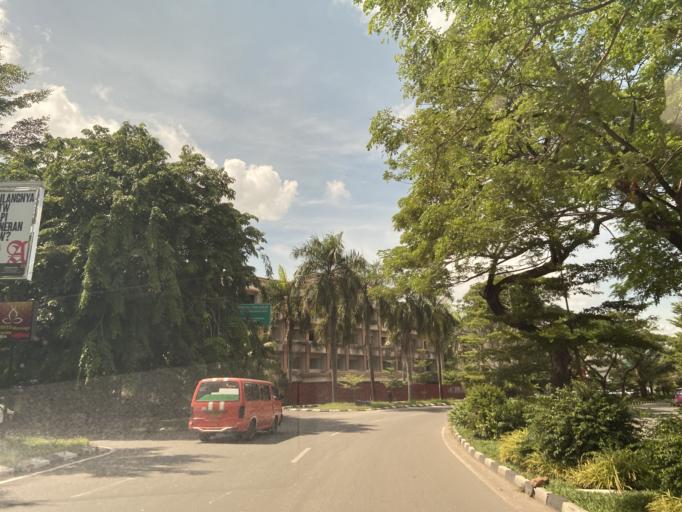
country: SG
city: Singapore
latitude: 1.1501
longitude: 104.0090
